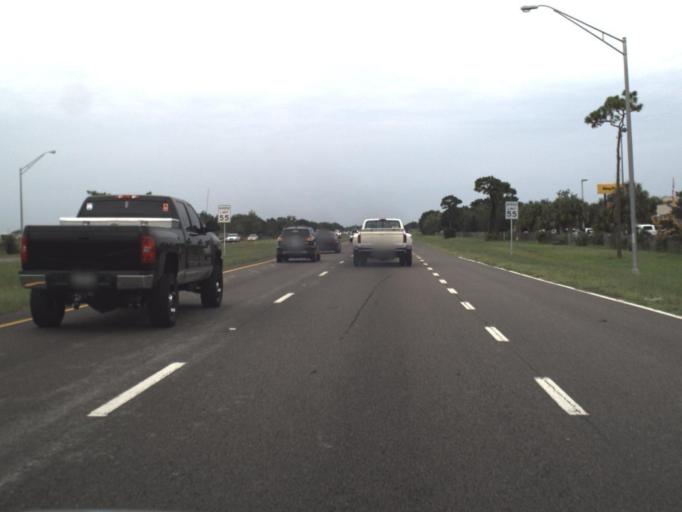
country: US
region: Florida
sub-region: Sarasota County
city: North Sarasota
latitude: 27.4041
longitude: -82.5328
